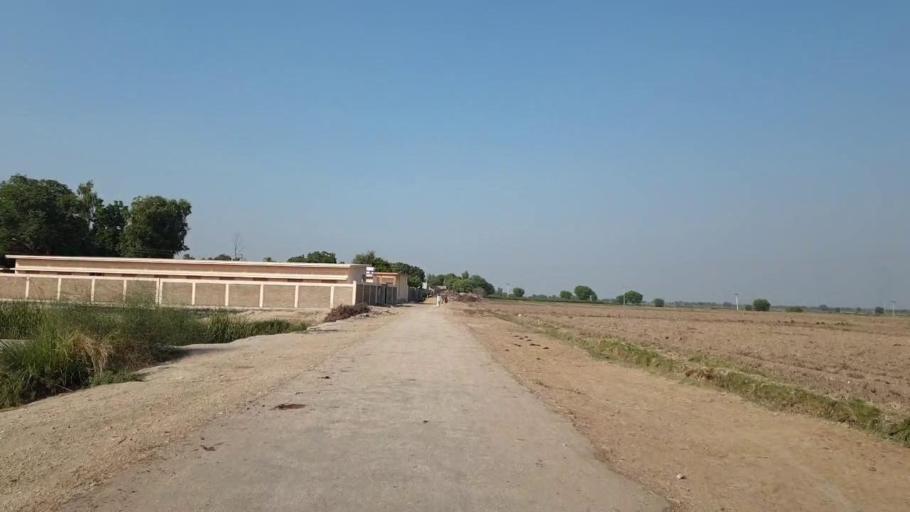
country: PK
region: Sindh
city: Sehwan
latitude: 26.4475
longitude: 67.8178
